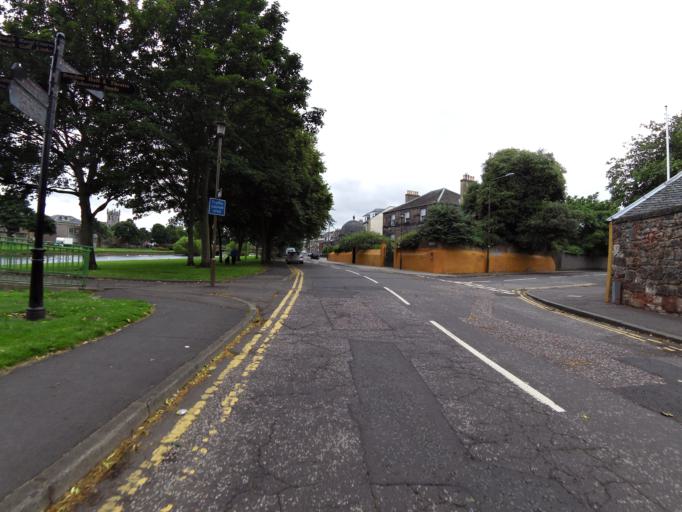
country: GB
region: Scotland
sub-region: East Lothian
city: Musselburgh
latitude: 55.9437
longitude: -3.0526
